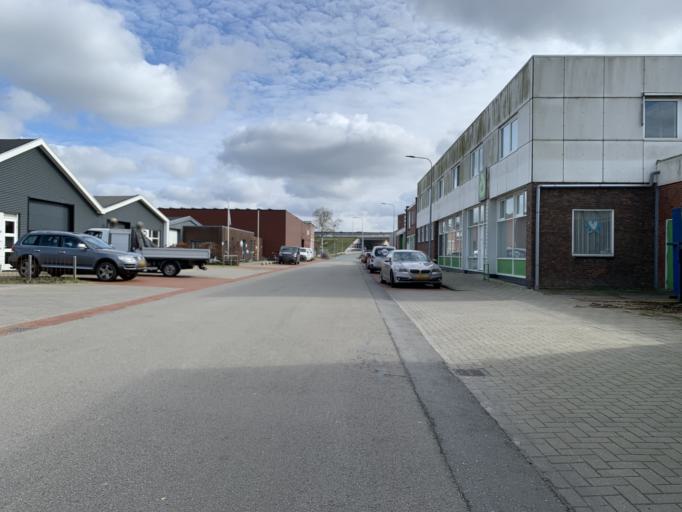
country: NL
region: Groningen
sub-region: Gemeente Groningen
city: Korrewegwijk
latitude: 53.2387
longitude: 6.5625
